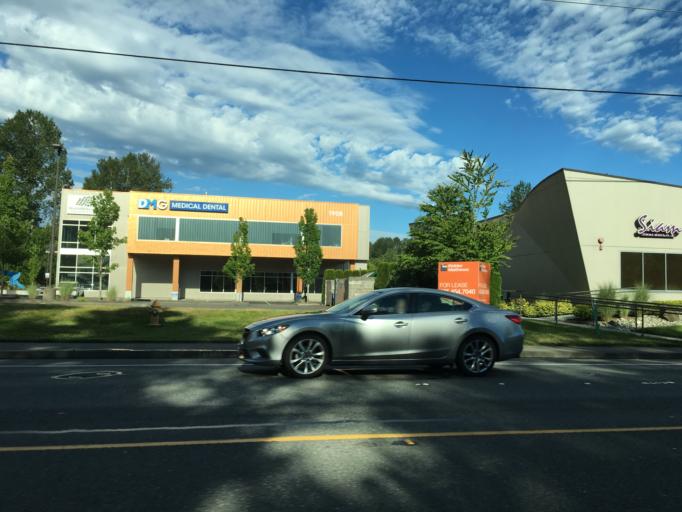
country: US
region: Washington
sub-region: Snohomish County
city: North Creek
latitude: 47.8157
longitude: -122.2076
